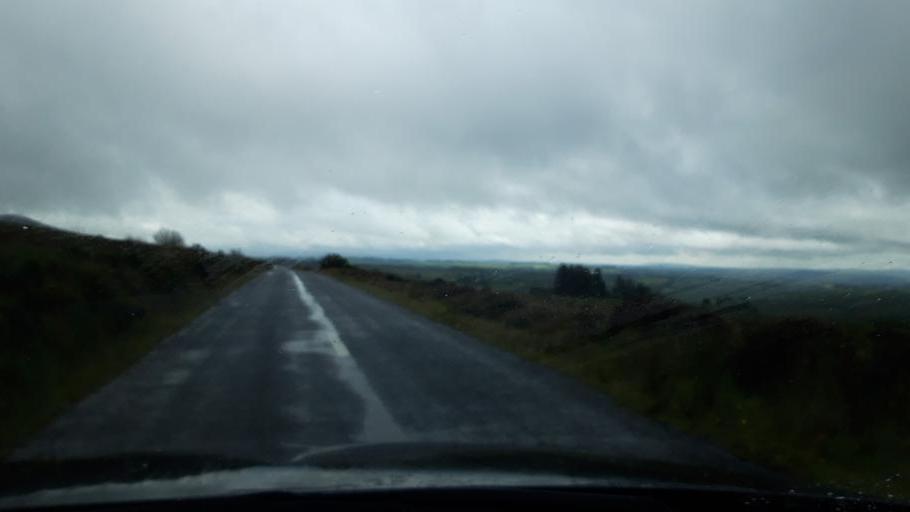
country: IE
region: Munster
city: Cahir
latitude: 52.2194
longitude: -7.9383
